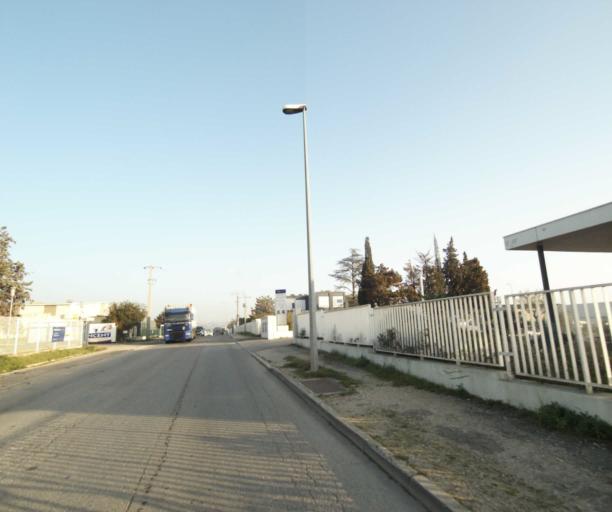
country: FR
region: Provence-Alpes-Cote d'Azur
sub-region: Departement des Bouches-du-Rhone
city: Vitrolles
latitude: 43.4381
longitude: 5.2464
